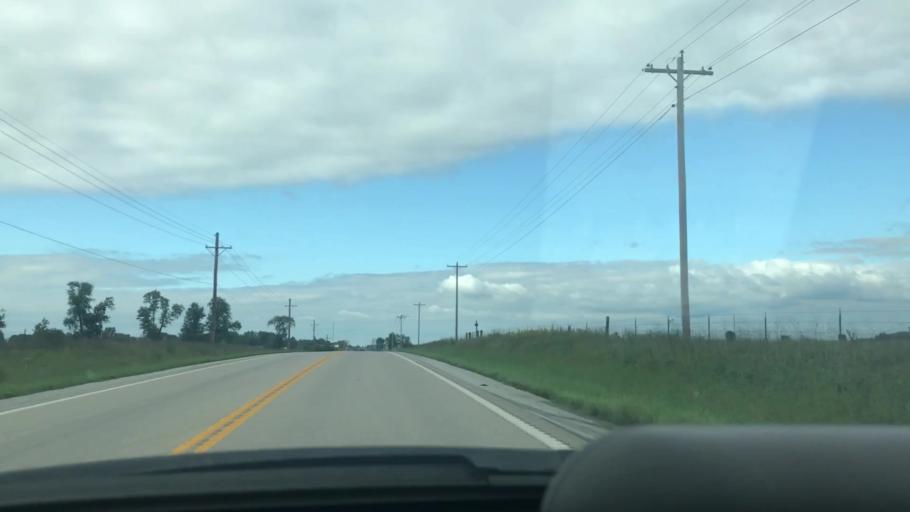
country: US
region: Missouri
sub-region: Hickory County
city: Hermitage
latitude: 37.9314
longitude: -93.2087
